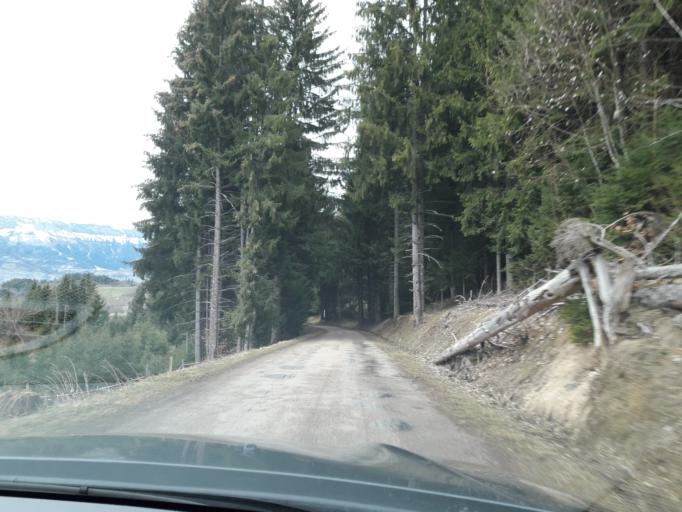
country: FR
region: Rhone-Alpes
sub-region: Departement de l'Isere
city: Le Champ-pres-Froges
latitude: 45.2438
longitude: 5.9796
